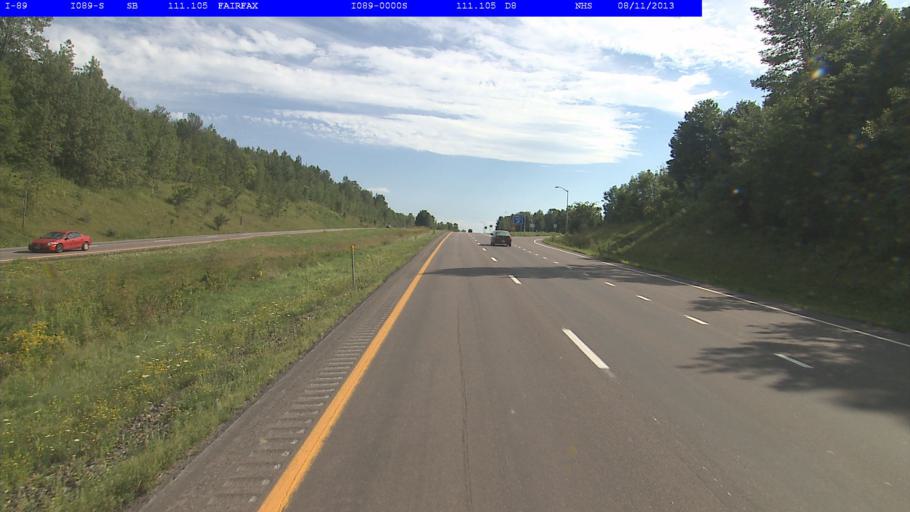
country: US
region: Vermont
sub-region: Franklin County
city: Saint Albans
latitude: 44.7572
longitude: -73.0772
